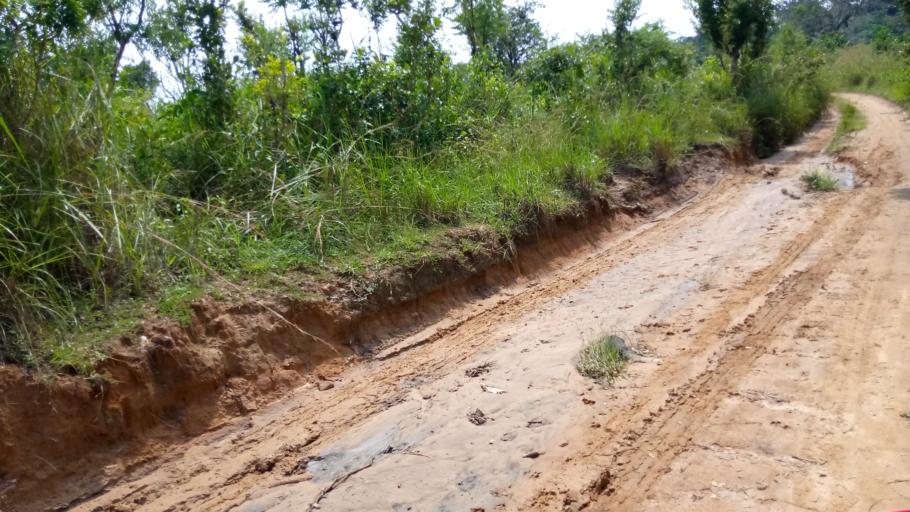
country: CD
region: Bandundu
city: Bandundu
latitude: -4.1365
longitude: 17.4166
